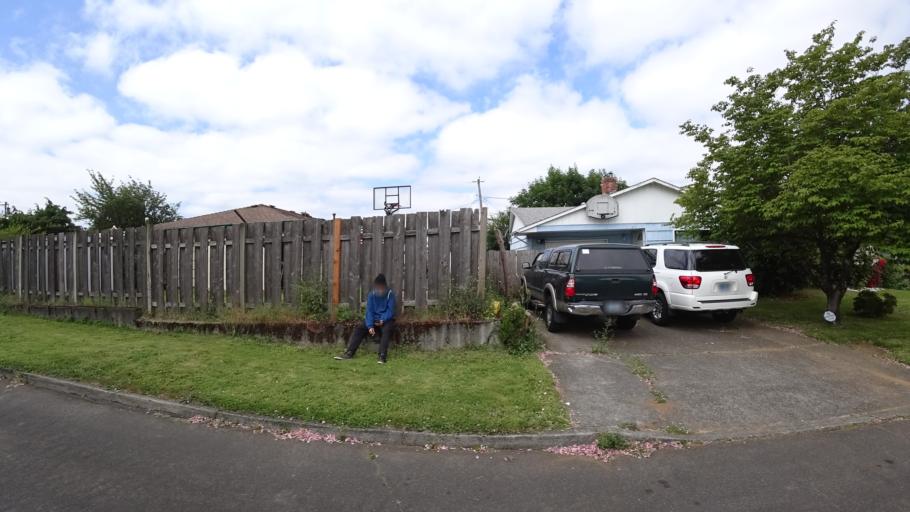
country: US
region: Oregon
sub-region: Multnomah County
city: Gresham
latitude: 45.4978
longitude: -122.4786
